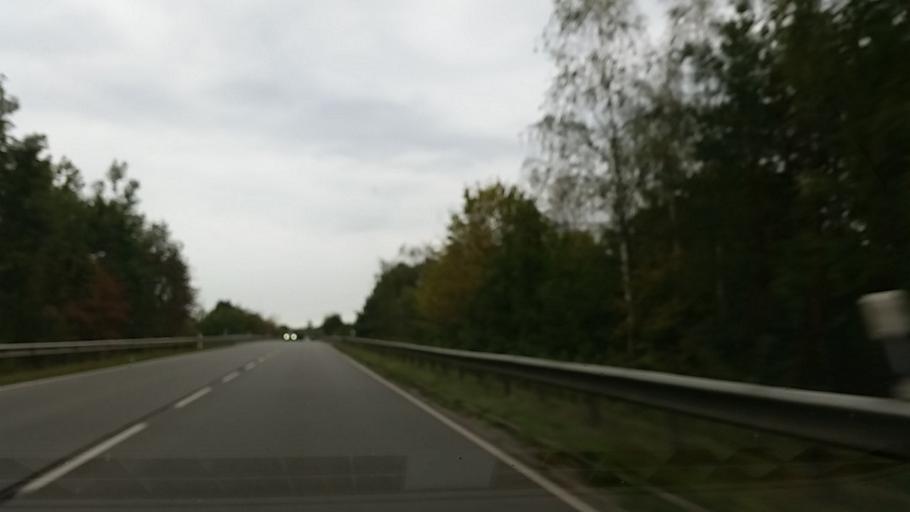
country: DE
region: Lower Saxony
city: Melbeck
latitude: 53.1954
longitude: 10.3769
